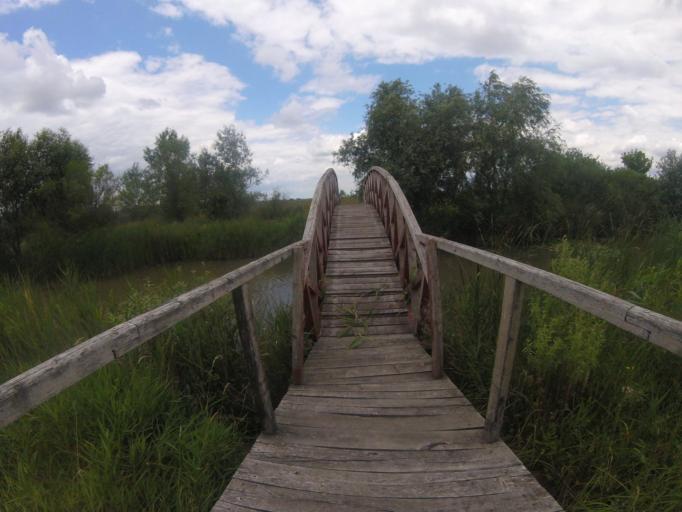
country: HU
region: Hajdu-Bihar
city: Egyek
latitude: 47.5691
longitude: 20.9378
